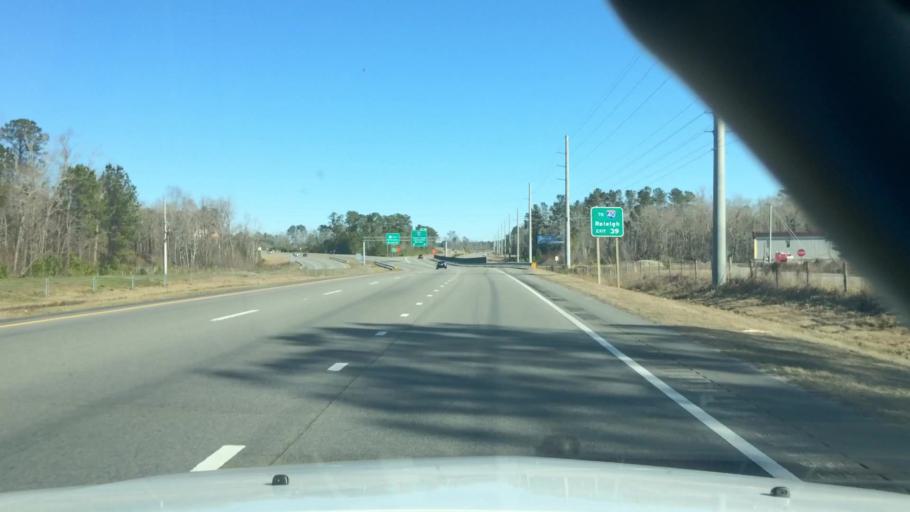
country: US
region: North Carolina
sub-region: Brunswick County
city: Leland
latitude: 34.1803
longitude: -78.0839
